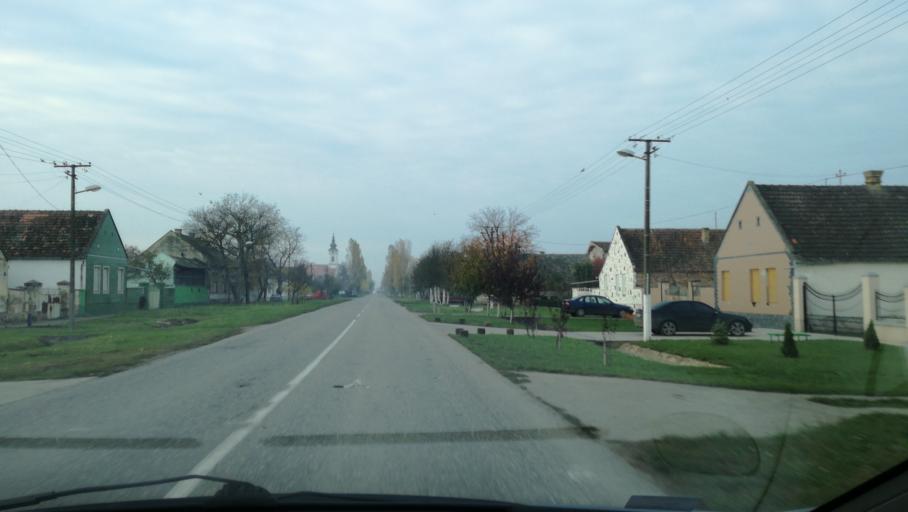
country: RS
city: Basaid
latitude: 45.6472
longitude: 20.4185
